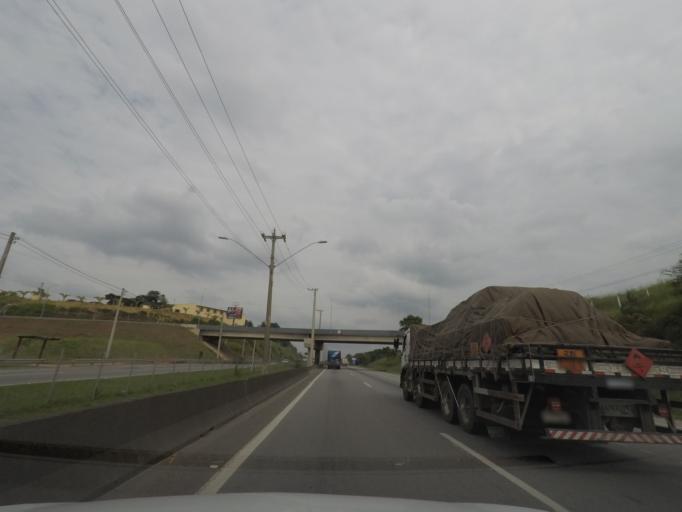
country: BR
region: Sao Paulo
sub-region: Itapecerica Da Serra
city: Itapecerica da Serra
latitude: -23.7069
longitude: -46.8746
